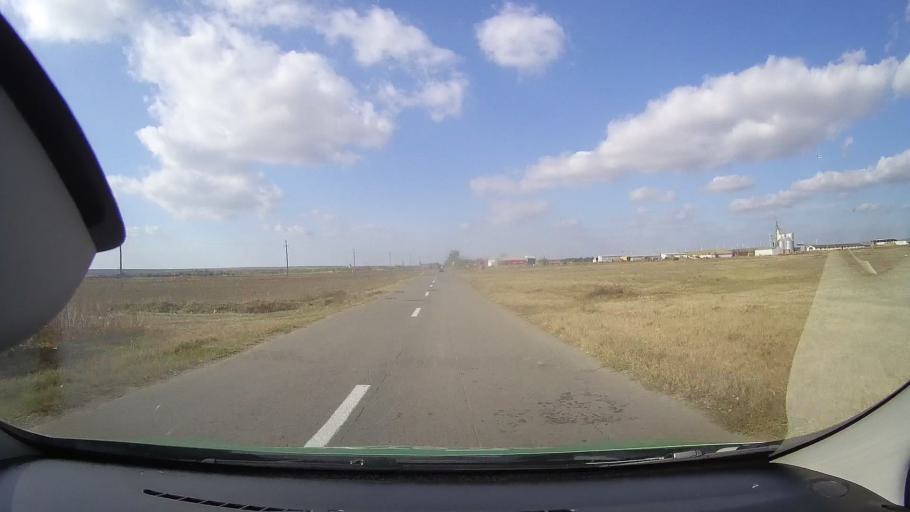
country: RO
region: Constanta
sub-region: Comuna Istria
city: Nuntasi
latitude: 44.5339
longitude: 28.6658
